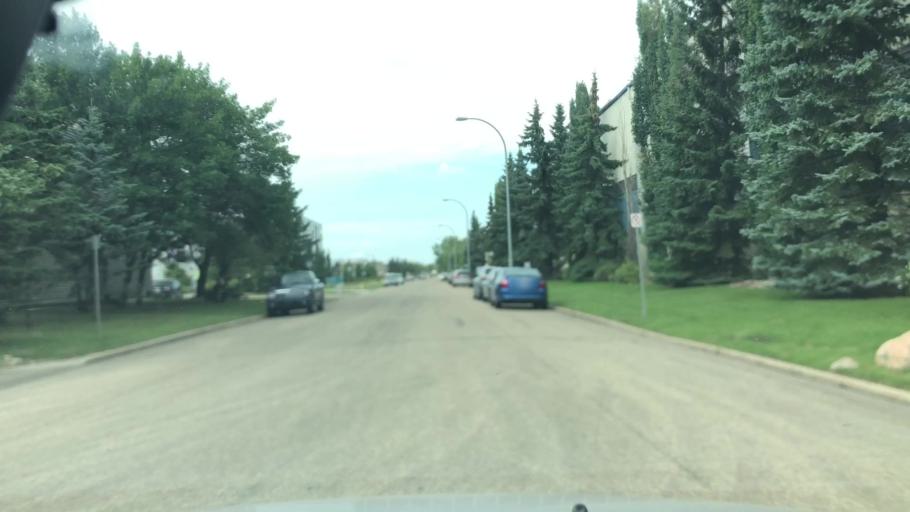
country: CA
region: Alberta
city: Edmonton
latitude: 53.5275
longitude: -113.4150
